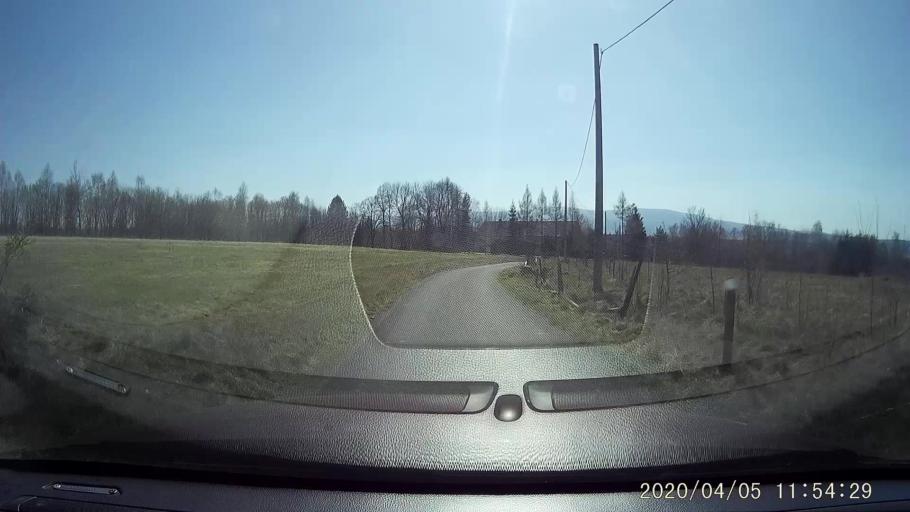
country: PL
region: Lower Silesian Voivodeship
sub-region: Powiat lubanski
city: Lesna
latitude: 50.9803
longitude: 15.3006
